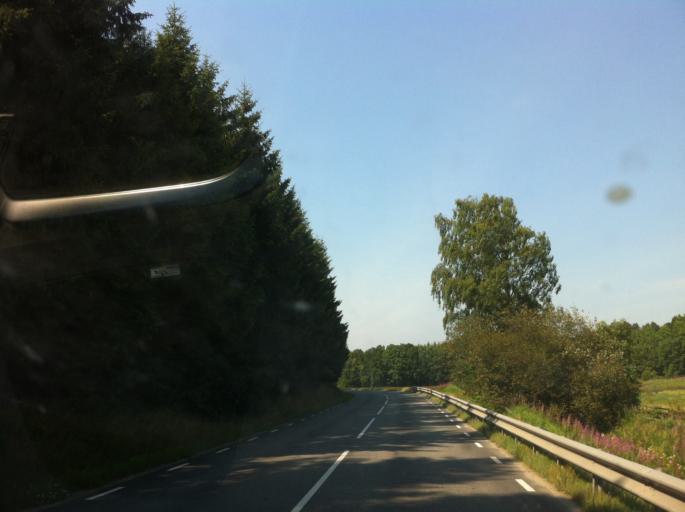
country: SE
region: Skane
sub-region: Hoors Kommun
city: Hoeoer
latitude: 56.0126
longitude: 13.5185
